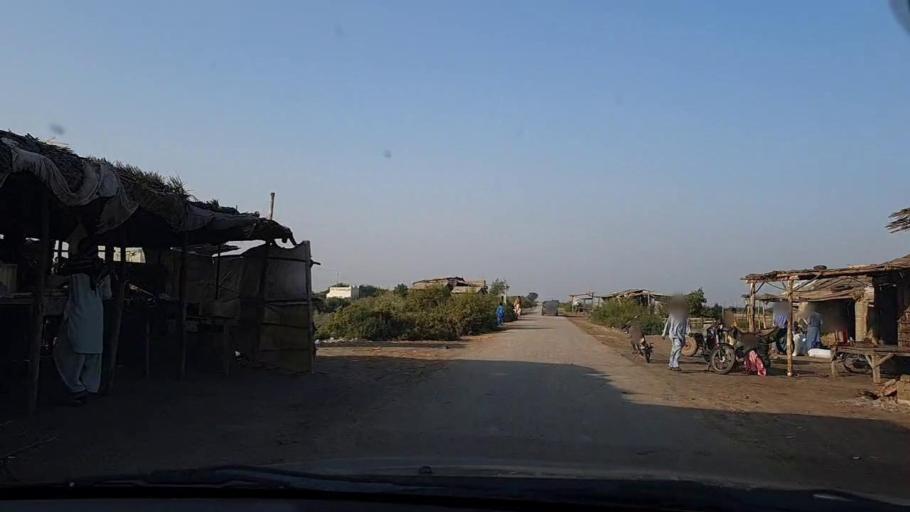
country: PK
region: Sindh
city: Chuhar Jamali
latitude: 24.3026
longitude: 67.7556
